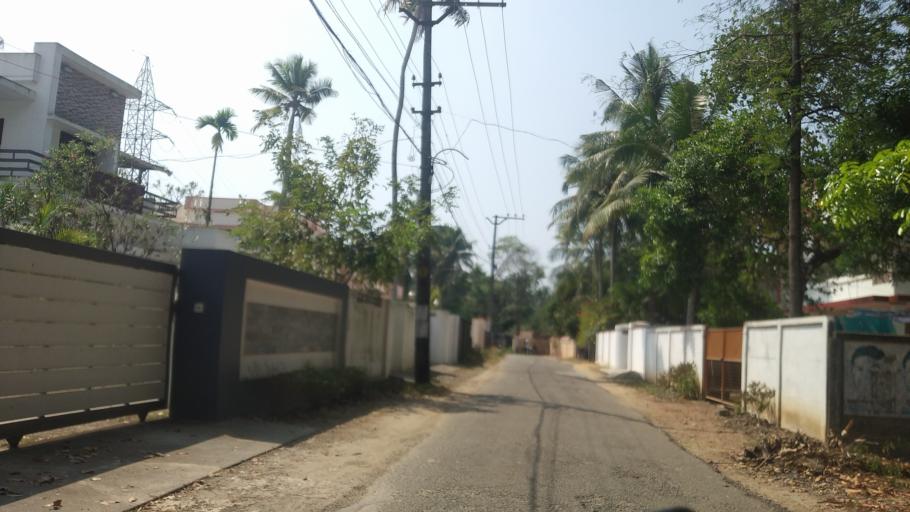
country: IN
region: Kerala
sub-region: Ernakulam
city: Elur
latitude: 10.1296
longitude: 76.2331
